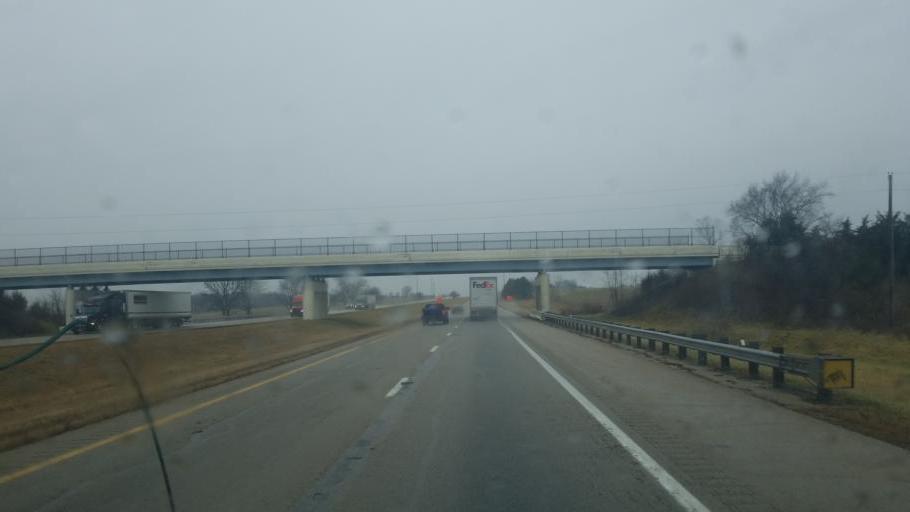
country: US
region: Ohio
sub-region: Preble County
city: New Paris
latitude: 39.8288
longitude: -84.7462
